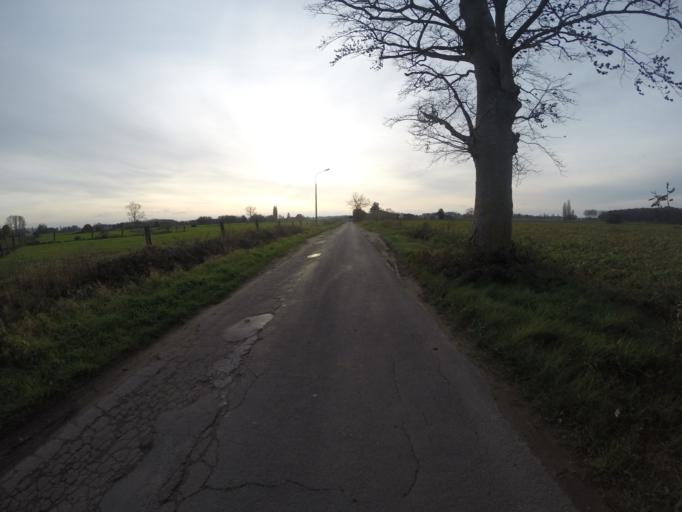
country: BE
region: Flanders
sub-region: Provincie Oost-Vlaanderen
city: Aalter
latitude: 51.0616
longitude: 3.4884
